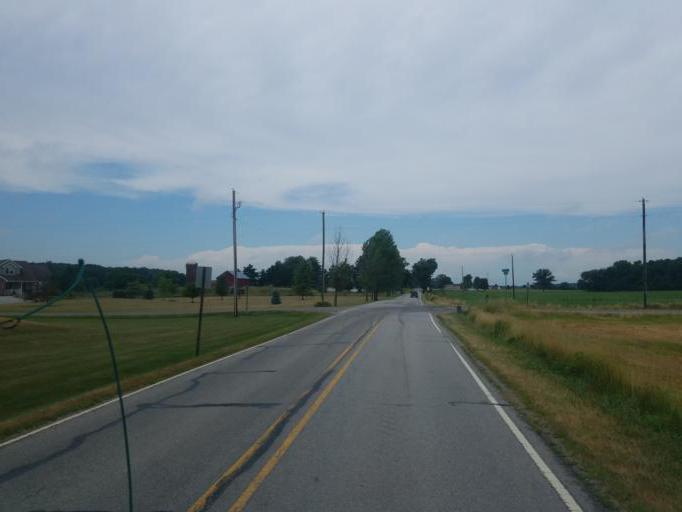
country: US
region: Indiana
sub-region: DeKalb County
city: Butler
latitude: 41.3861
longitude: -84.8499
